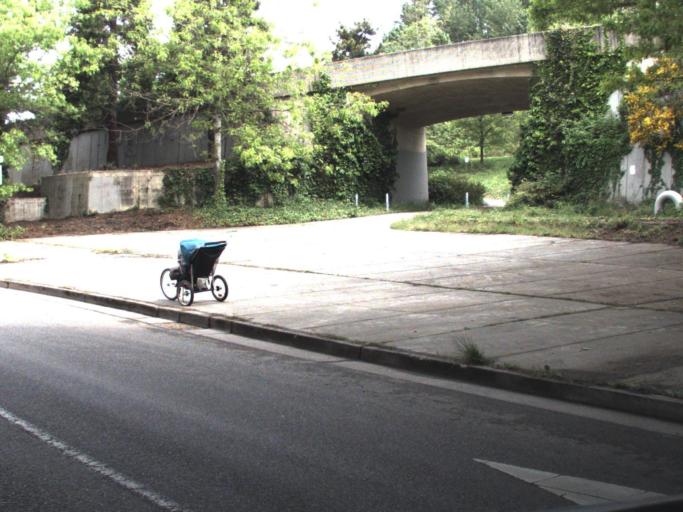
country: US
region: Washington
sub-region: King County
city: Seattle
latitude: 47.5927
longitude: -122.3290
